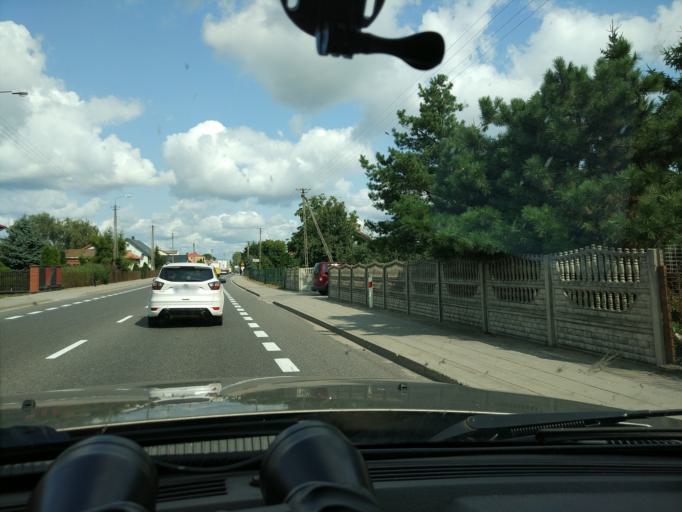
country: PL
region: Masovian Voivodeship
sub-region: Powiat mlawski
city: Wisniewo
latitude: 53.0622
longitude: 20.3474
